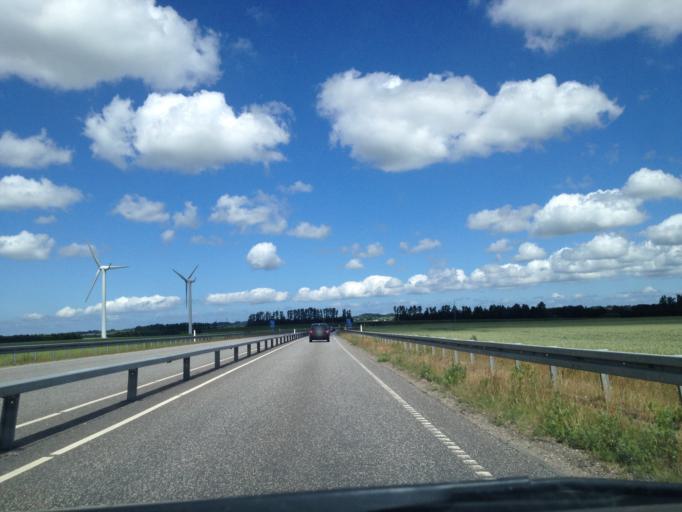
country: DK
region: Zealand
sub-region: Odsherred Kommune
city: Asnaes
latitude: 55.7587
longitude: 11.5806
